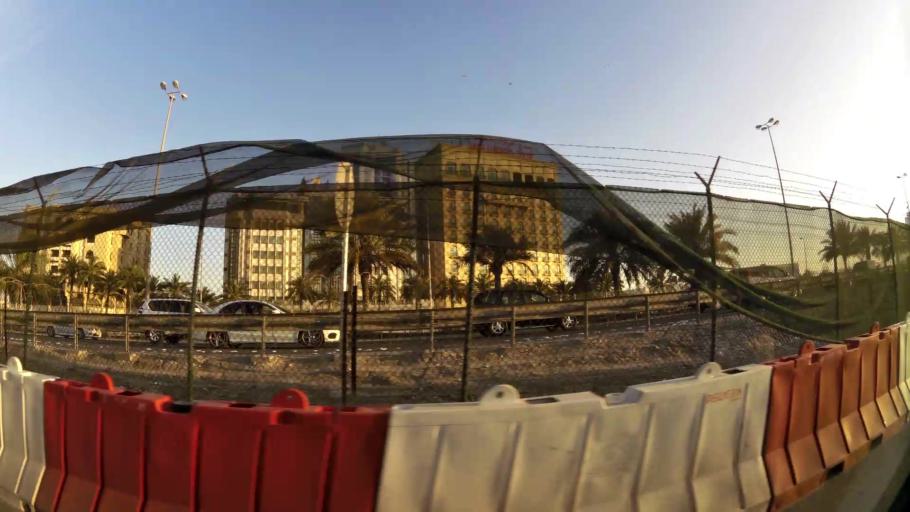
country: BH
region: Manama
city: Jidd Hafs
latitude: 26.2333
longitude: 50.5647
